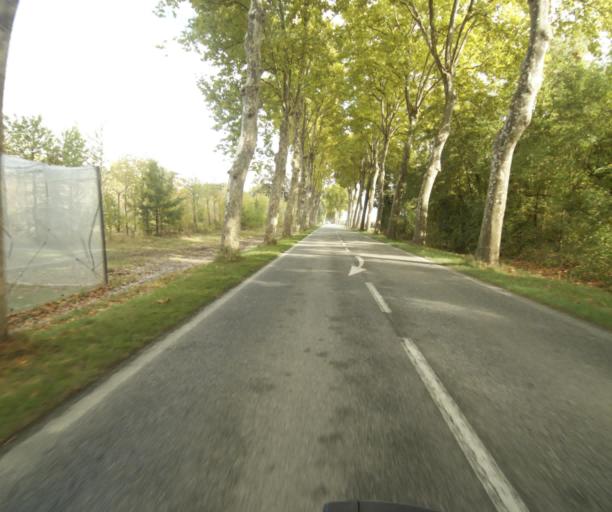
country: FR
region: Midi-Pyrenees
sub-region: Departement du Tarn-et-Garonne
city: Montech
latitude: 43.9531
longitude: 1.1846
